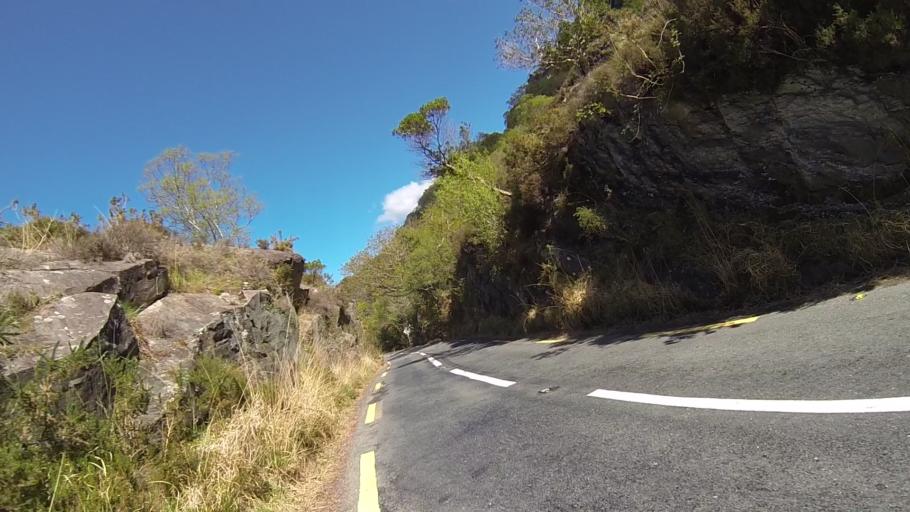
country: IE
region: Munster
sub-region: Ciarrai
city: Cill Airne
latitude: 51.9825
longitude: -9.5707
